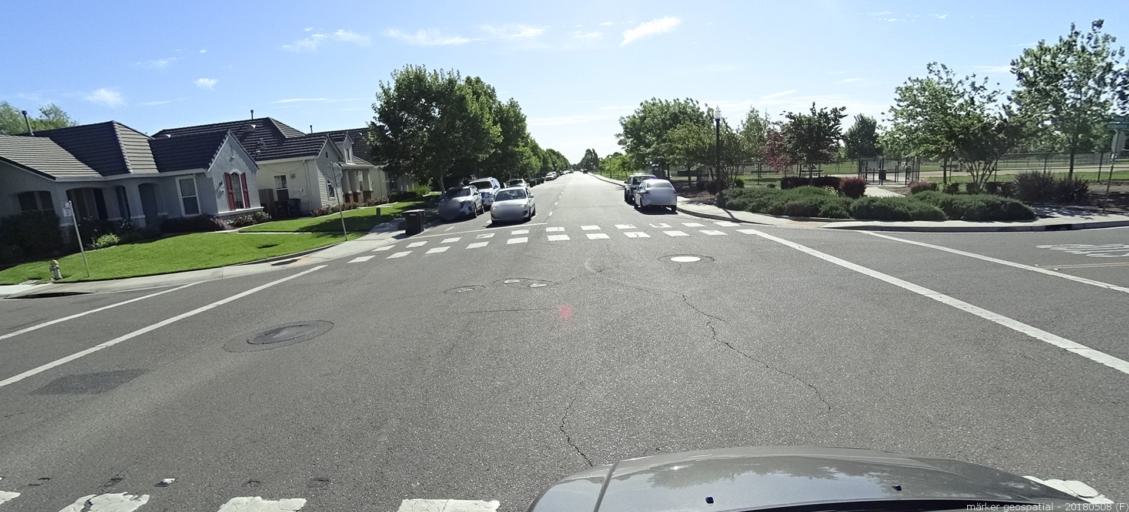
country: US
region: California
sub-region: Sacramento County
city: Elverta
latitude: 38.6819
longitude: -121.5056
